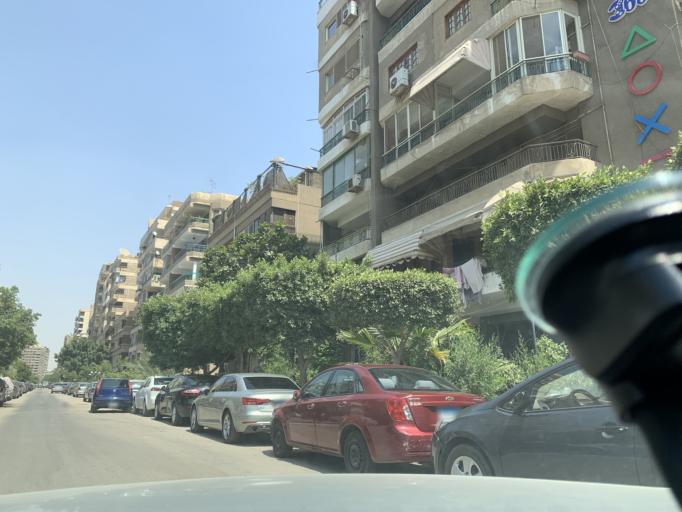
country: EG
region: Muhafazat al Qahirah
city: Cairo
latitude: 30.0600
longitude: 31.3499
